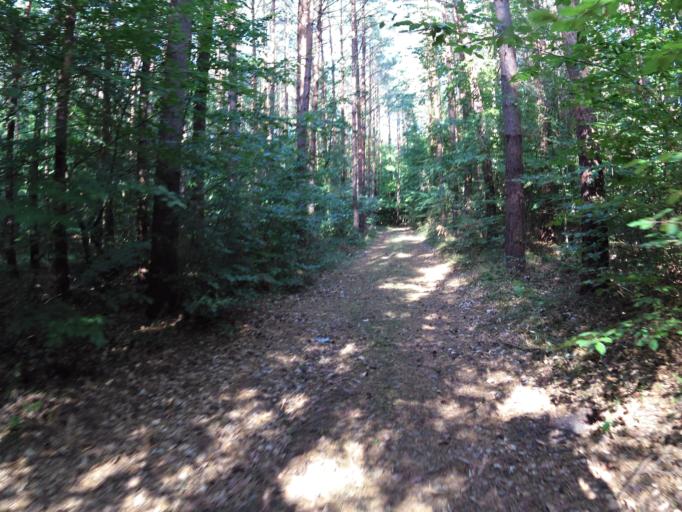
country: DE
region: Mecklenburg-Vorpommern
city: Loddin
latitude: 54.0065
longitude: 14.0540
